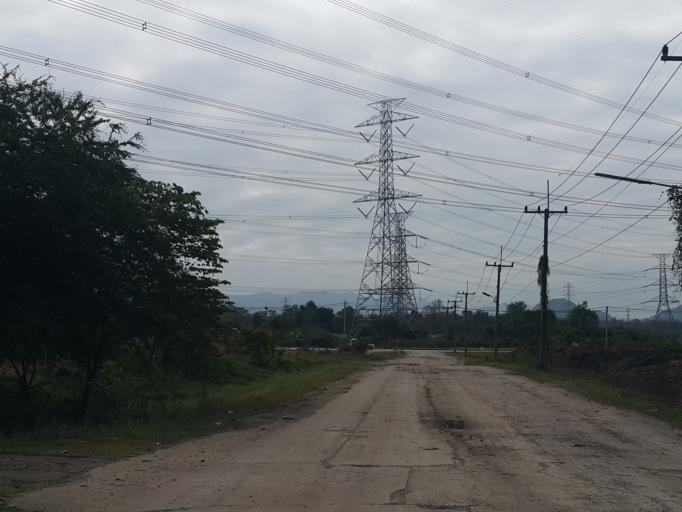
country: TH
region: Lampang
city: Mae Mo
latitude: 18.2942
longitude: 99.7400
